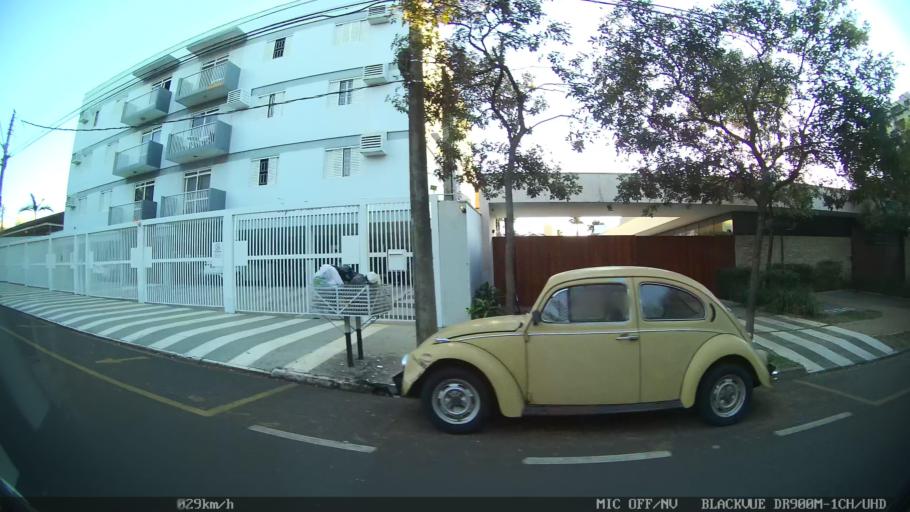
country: BR
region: Sao Paulo
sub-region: Sao Jose Do Rio Preto
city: Sao Jose do Rio Preto
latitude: -20.8469
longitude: -49.3943
